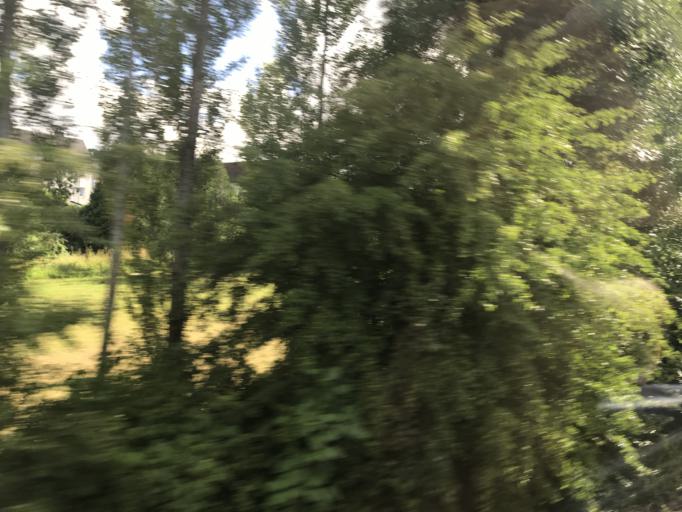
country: LU
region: Luxembourg
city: Rodange
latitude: 49.5506
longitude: 5.8361
